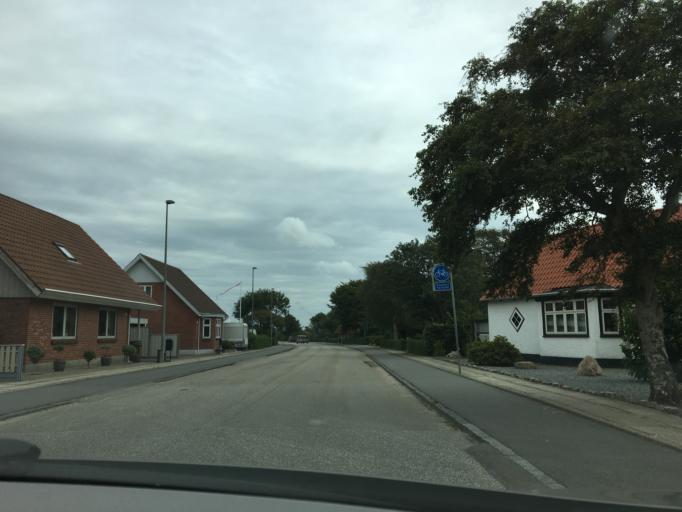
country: DK
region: Central Jutland
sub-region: Ringkobing-Skjern Kommune
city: Ringkobing
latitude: 56.0825
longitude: 8.2571
